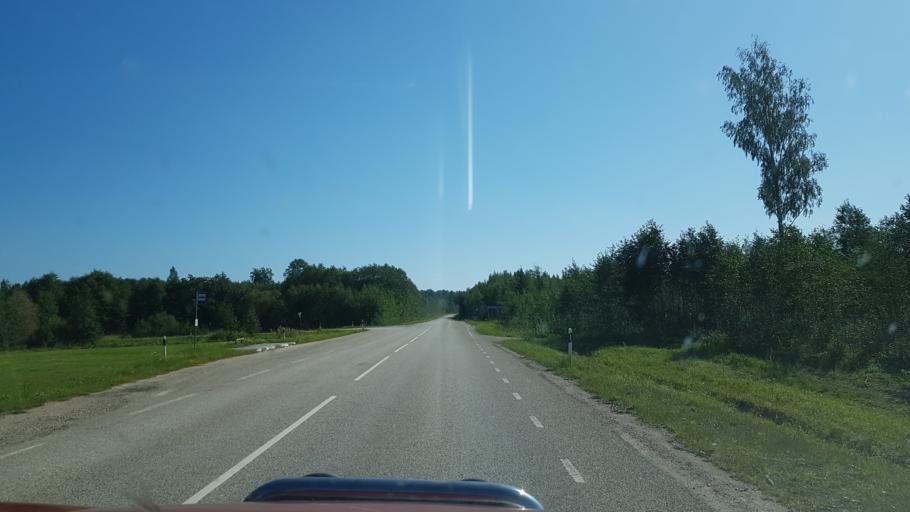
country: EE
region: Polvamaa
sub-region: Polva linn
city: Polva
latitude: 58.2654
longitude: 27.1628
